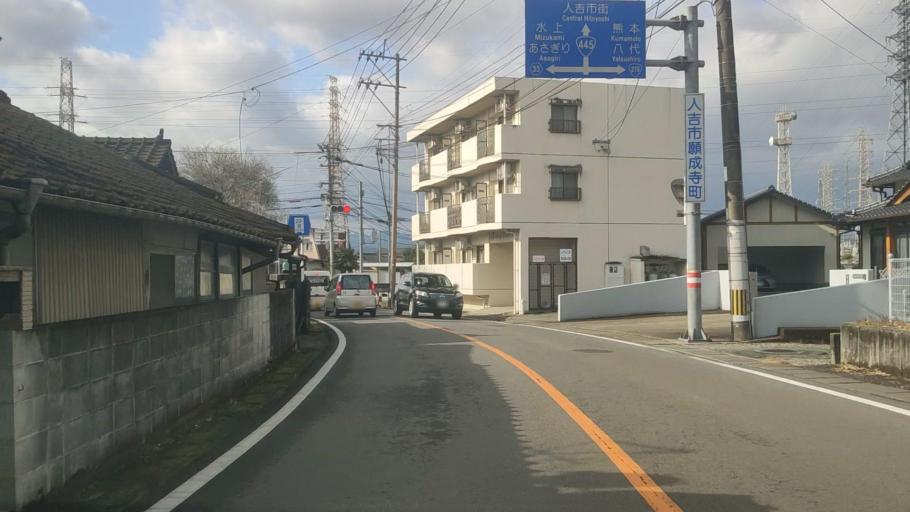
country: JP
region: Kumamoto
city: Hitoyoshi
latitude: 32.2228
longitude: 130.7752
